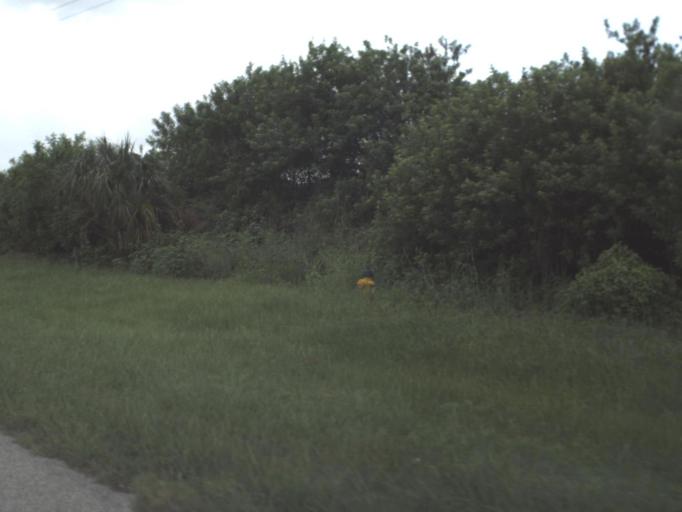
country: US
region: Florida
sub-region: Hillsborough County
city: Sun City Center
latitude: 27.7280
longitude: -82.3353
